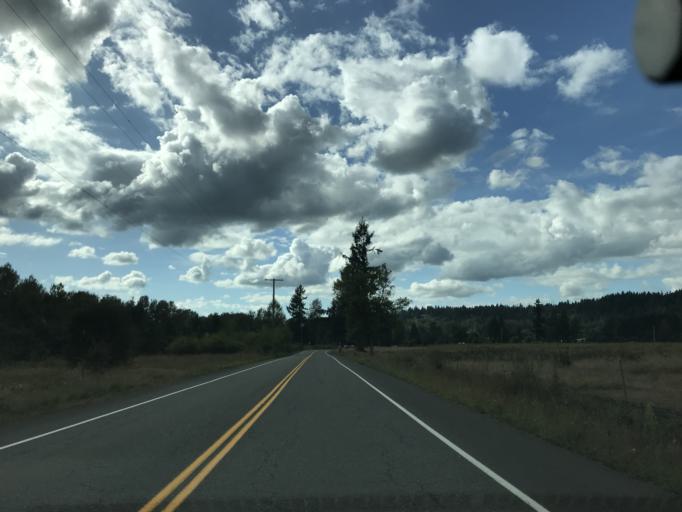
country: US
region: Washington
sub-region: King County
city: Black Diamond
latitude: 47.2822
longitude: -122.0493
